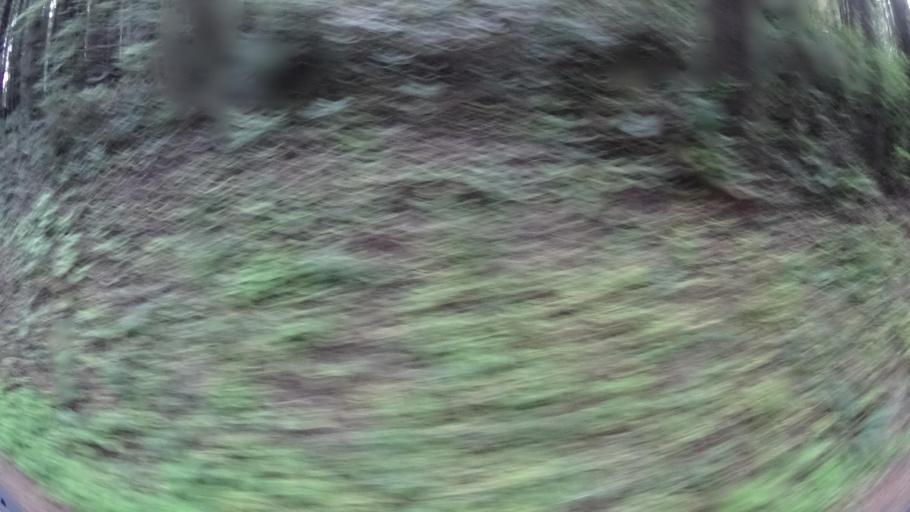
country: US
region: California
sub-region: Humboldt County
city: Bayside
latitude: 40.7553
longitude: -124.0483
